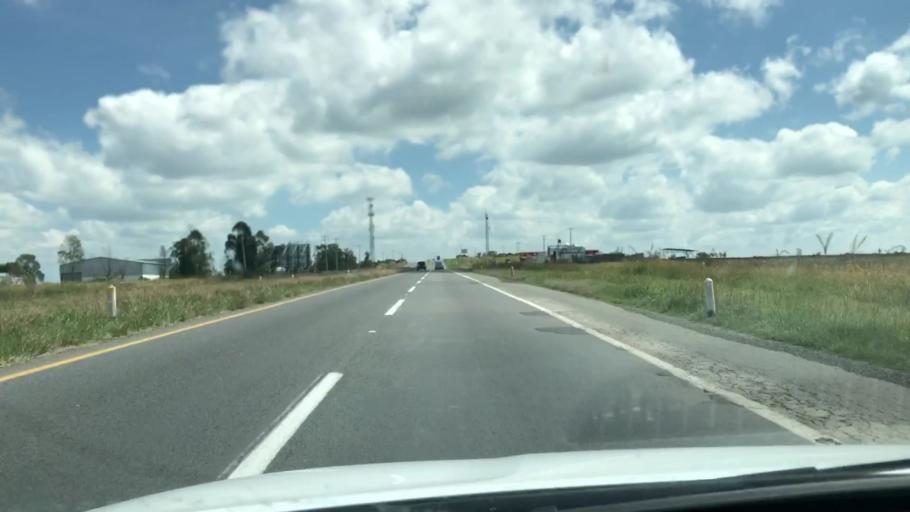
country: MX
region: Jalisco
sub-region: San Juan de los Lagos
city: Mezquitic de la Magdalena
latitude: 21.2931
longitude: -102.1548
